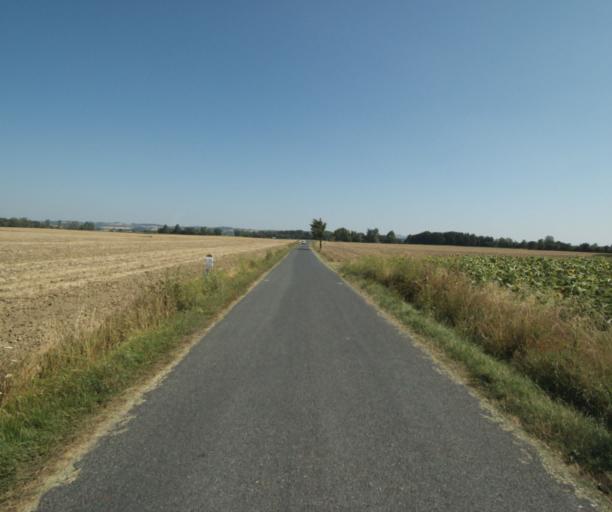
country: FR
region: Midi-Pyrenees
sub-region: Departement de la Haute-Garonne
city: Revel
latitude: 43.5097
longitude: 1.9520
